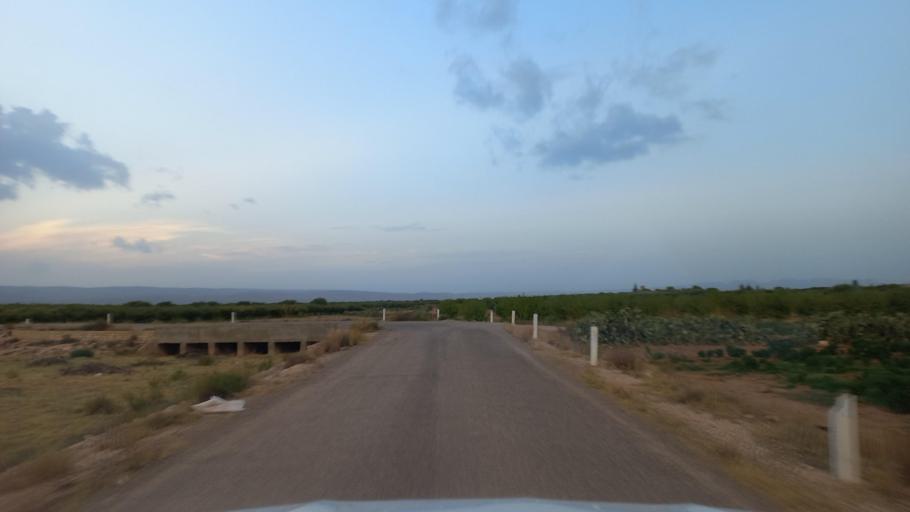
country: TN
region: Al Qasrayn
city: Kasserine
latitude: 35.2744
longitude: 9.0436
